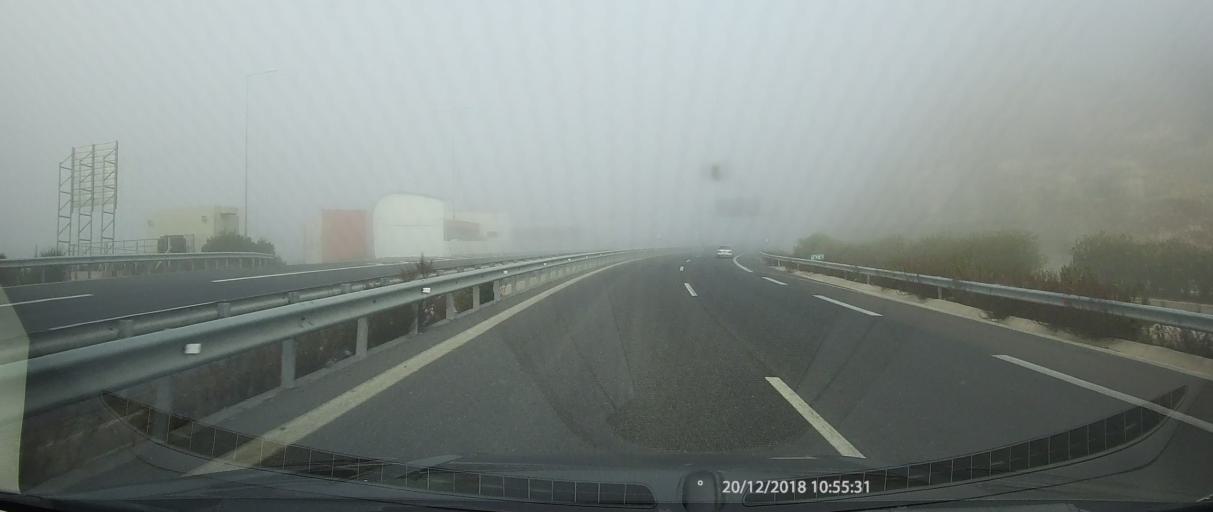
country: GR
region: Peloponnese
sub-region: Nomos Arkadias
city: Tripoli
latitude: 37.6497
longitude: 22.4655
